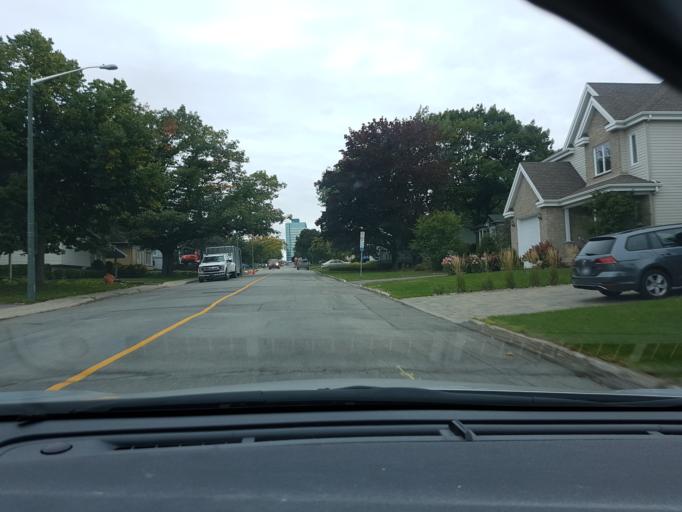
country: CA
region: Quebec
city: Quebec
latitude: 46.7661
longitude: -71.2759
